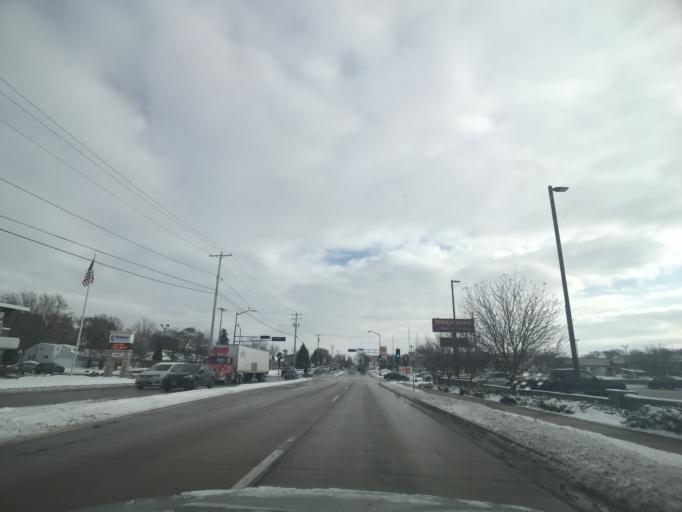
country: US
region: Wisconsin
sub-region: Brown County
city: De Pere
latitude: 44.4507
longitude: -88.0843
